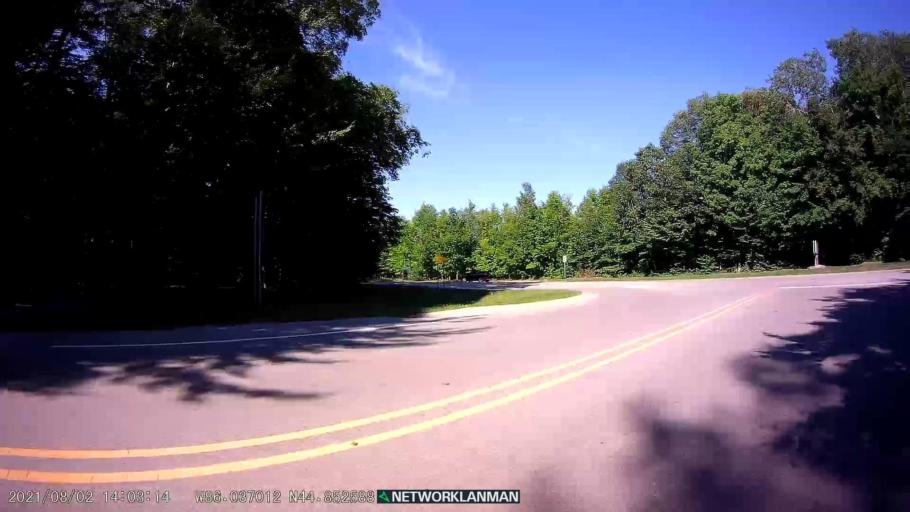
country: US
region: Michigan
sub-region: Benzie County
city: Beulah
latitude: 44.8527
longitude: -86.0368
